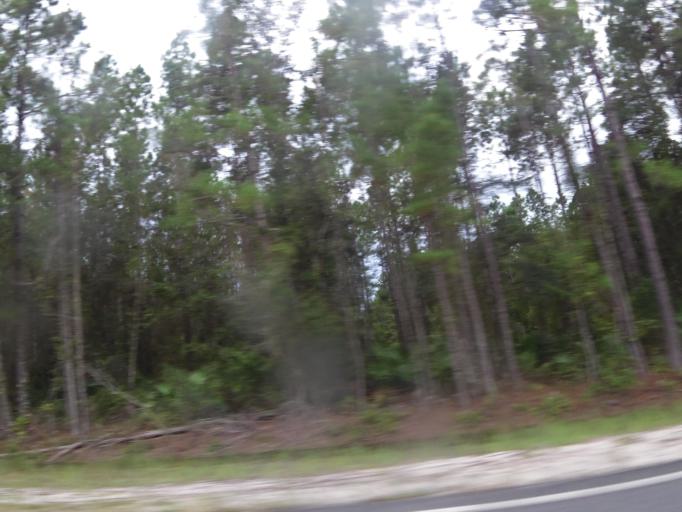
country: US
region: Florida
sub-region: Baker County
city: Macclenny
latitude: 30.5074
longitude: -82.2146
